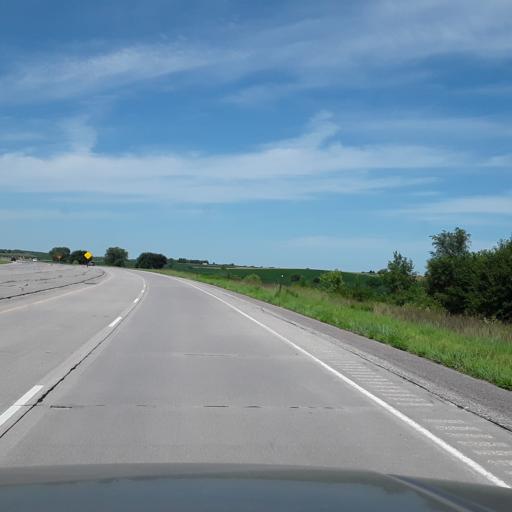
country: US
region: Nebraska
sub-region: Lancaster County
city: Lincoln
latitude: 40.8882
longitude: -96.7998
